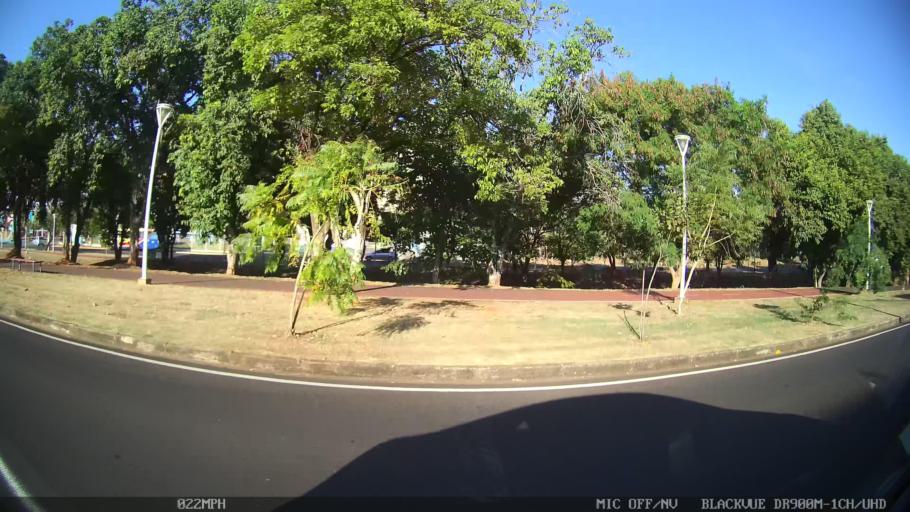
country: BR
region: Sao Paulo
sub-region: Sao Jose Do Rio Preto
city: Sao Jose do Rio Preto
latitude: -20.8277
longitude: -49.4045
